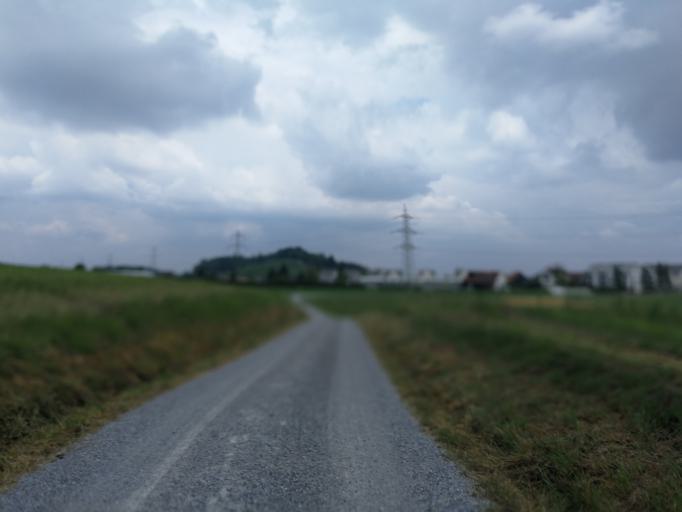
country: CH
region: Zurich
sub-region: Bezirk Hinwil
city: Binzikon
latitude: 47.2714
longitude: 8.7565
